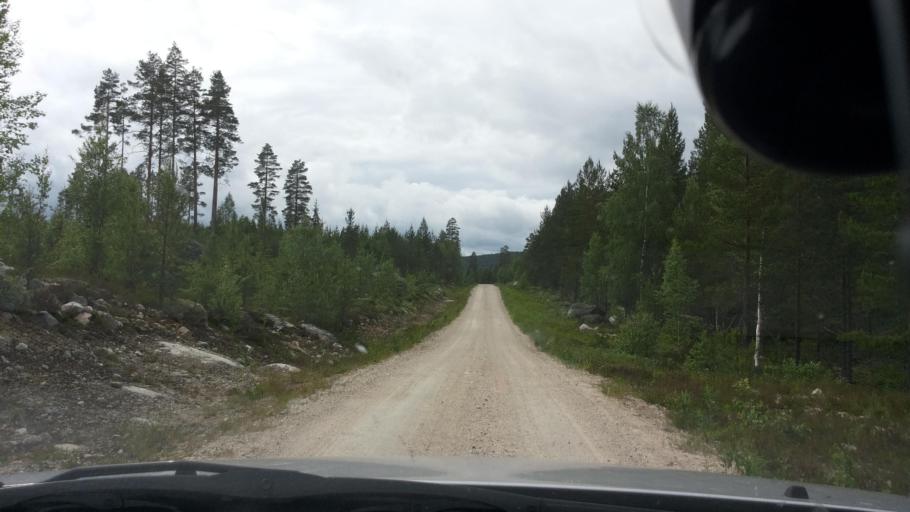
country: SE
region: Gaevleborg
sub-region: Ovanakers Kommun
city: Edsbyn
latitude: 61.4864
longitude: 15.3174
